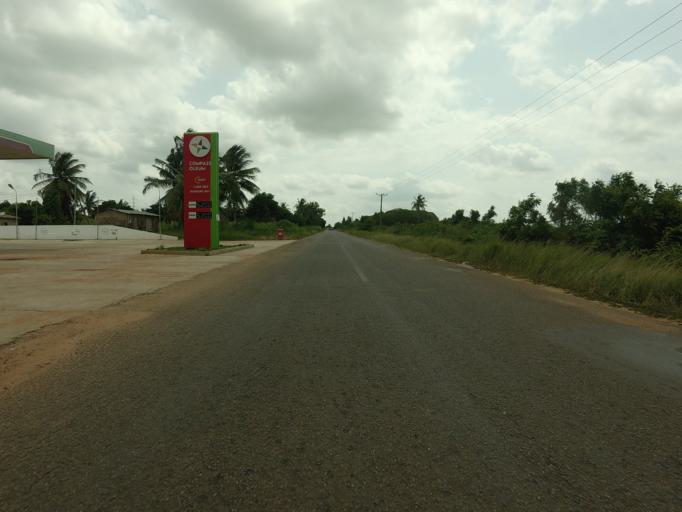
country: TG
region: Maritime
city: Lome
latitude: 6.1720
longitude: 1.0768
